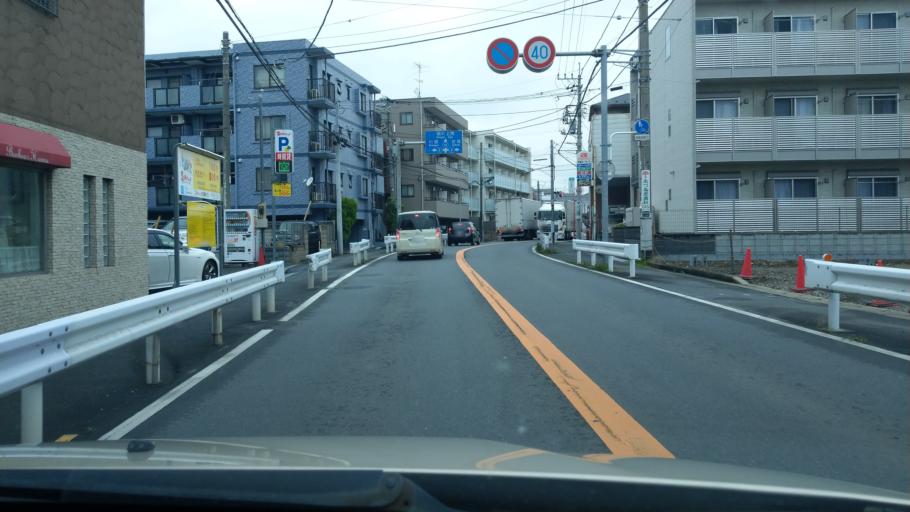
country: JP
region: Saitama
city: Saitama
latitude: 35.9104
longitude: 139.6338
